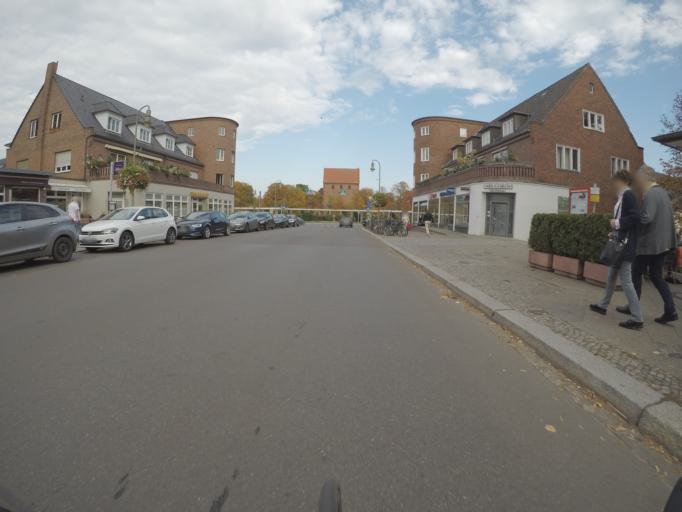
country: DE
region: Berlin
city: Frohnau
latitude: 52.6332
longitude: 13.2898
